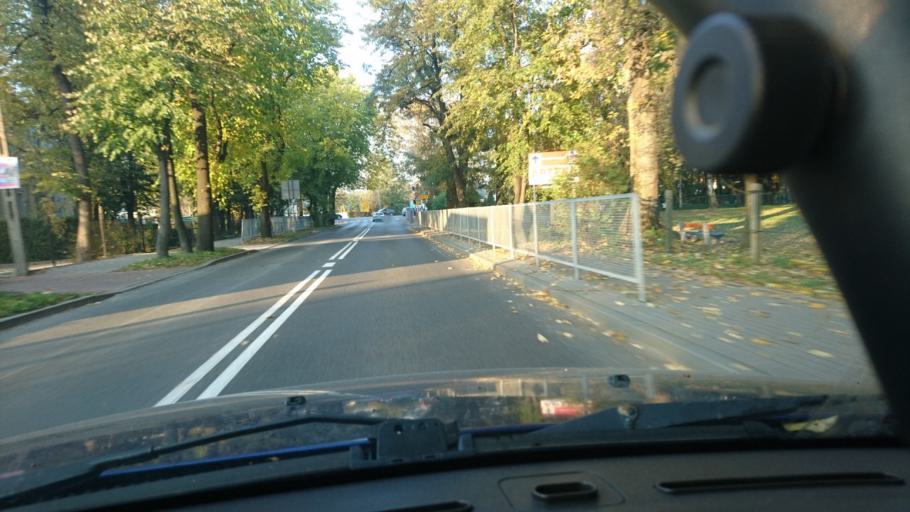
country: PL
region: Silesian Voivodeship
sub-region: Powiat bielski
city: Jaworze
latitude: 49.8070
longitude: 18.9822
